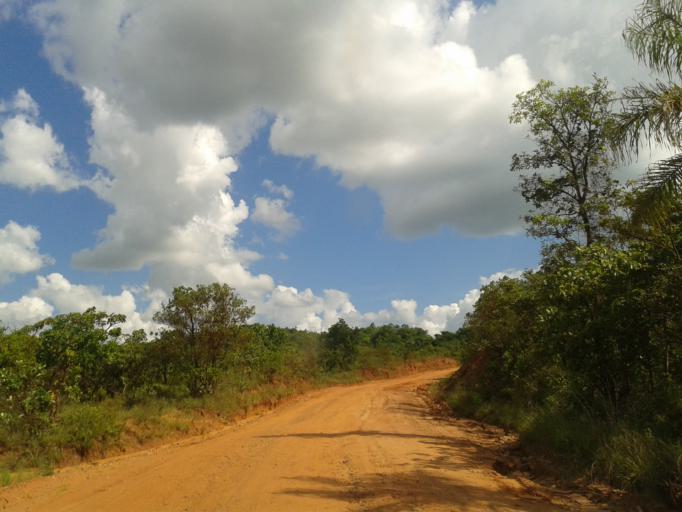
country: BR
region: Minas Gerais
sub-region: Campina Verde
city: Campina Verde
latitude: -19.3228
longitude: -49.8016
